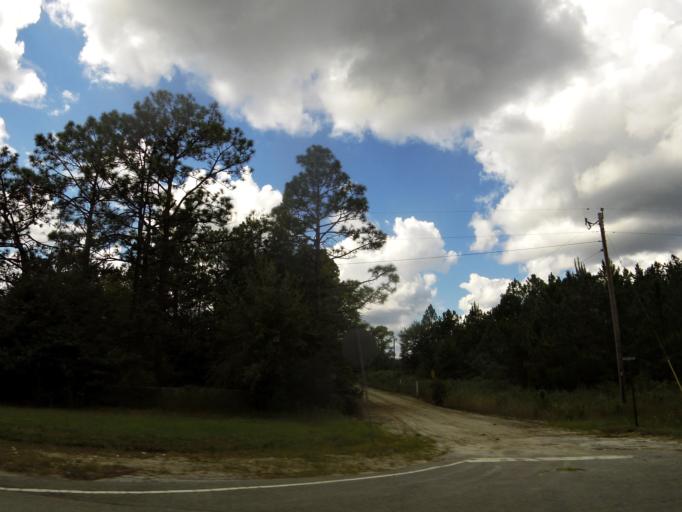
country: US
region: Georgia
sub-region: Charlton County
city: Folkston
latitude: 30.8943
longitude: -82.0163
